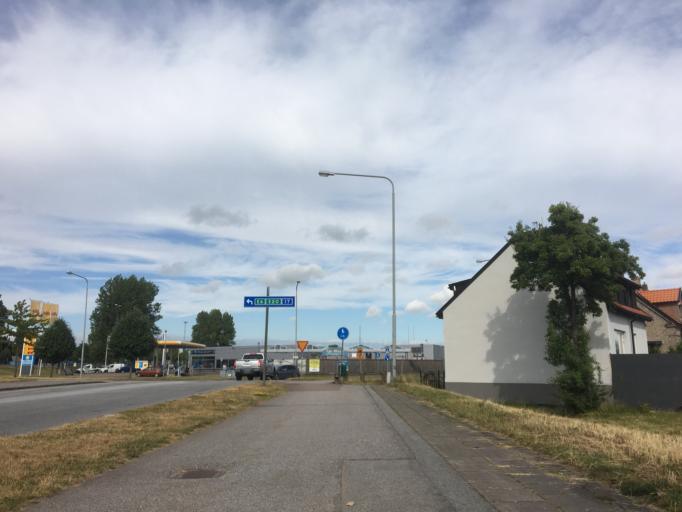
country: SE
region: Skane
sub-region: Landskrona
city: Landskrona
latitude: 55.8713
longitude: 12.8542
